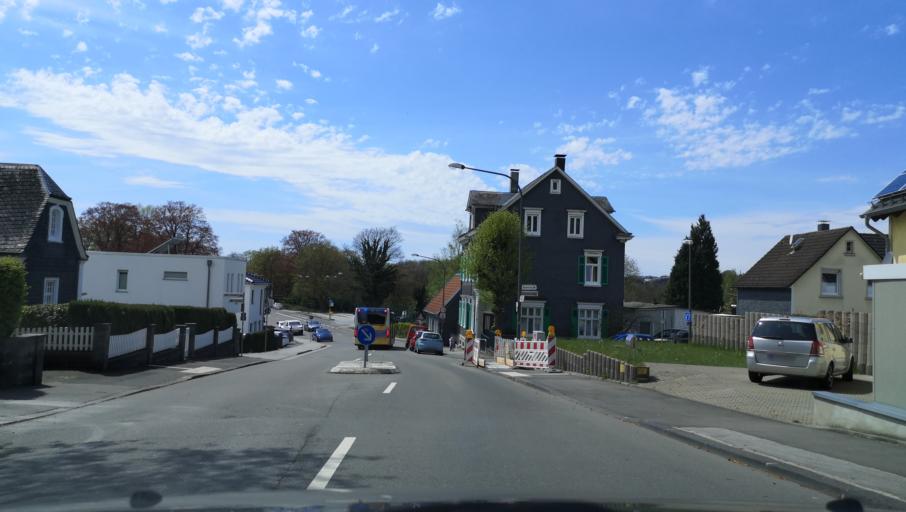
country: DE
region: North Rhine-Westphalia
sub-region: Regierungsbezirk Dusseldorf
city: Remscheid
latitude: 51.1595
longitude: 7.1705
